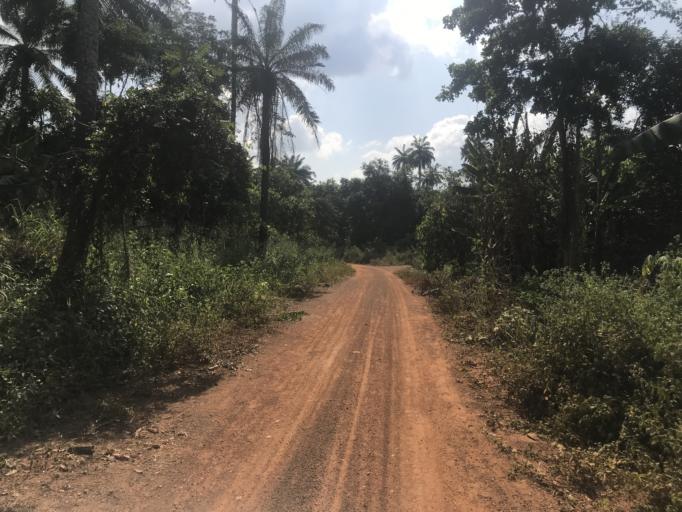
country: NG
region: Osun
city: Ibokun
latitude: 7.8100
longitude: 4.6936
